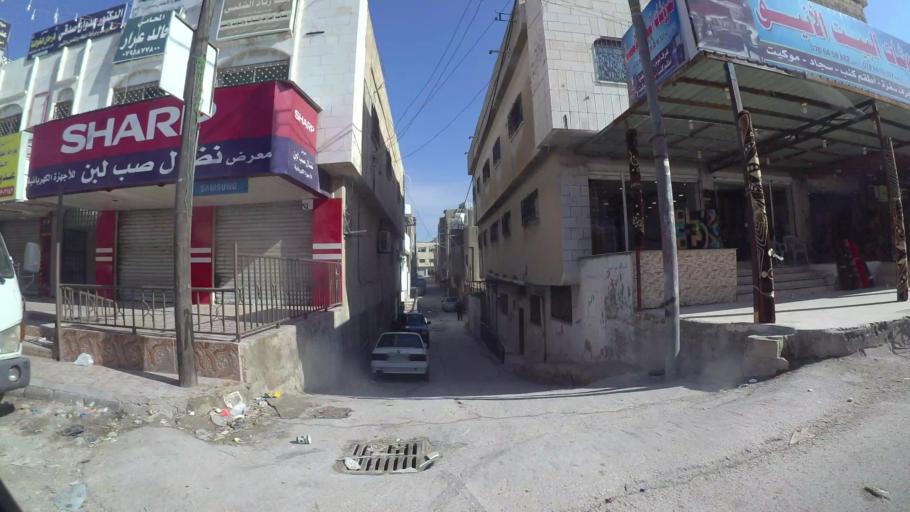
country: JO
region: Amman
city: Al Jubayhah
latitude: 32.0767
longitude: 35.8412
